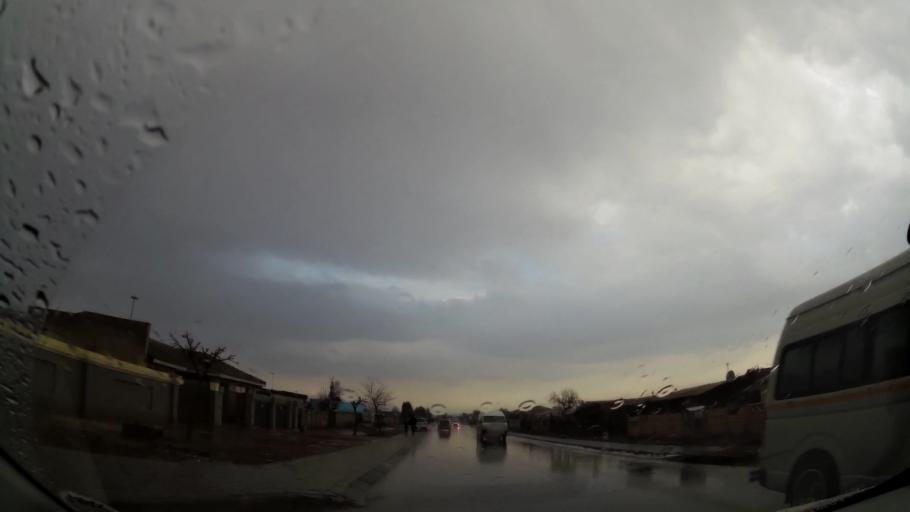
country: ZA
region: Gauteng
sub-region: Ekurhuleni Metropolitan Municipality
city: Germiston
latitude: -26.3564
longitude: 28.1410
